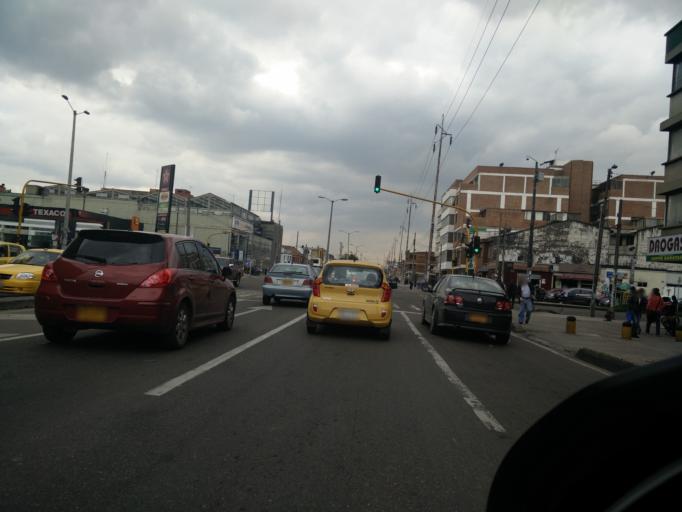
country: CO
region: Bogota D.C.
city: Bogota
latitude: 4.6510
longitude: -74.0721
